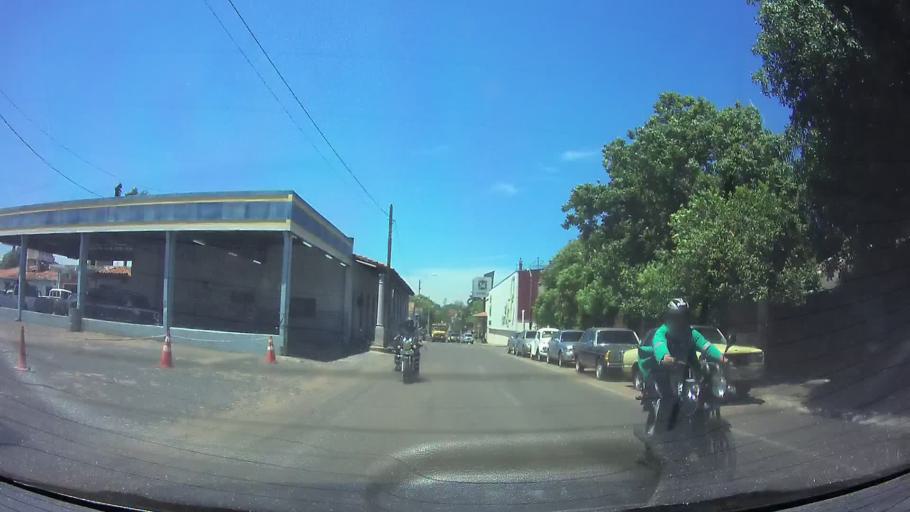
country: PY
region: Central
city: San Lorenzo
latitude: -25.2617
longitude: -57.4893
